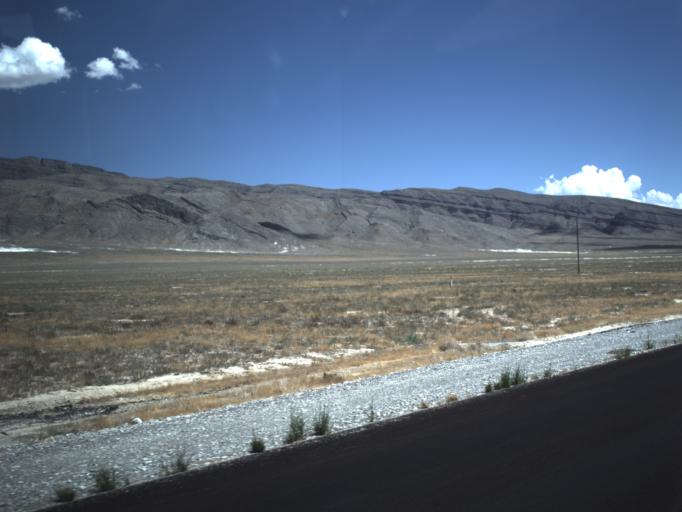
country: US
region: Utah
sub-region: Beaver County
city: Milford
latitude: 39.0707
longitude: -113.4623
